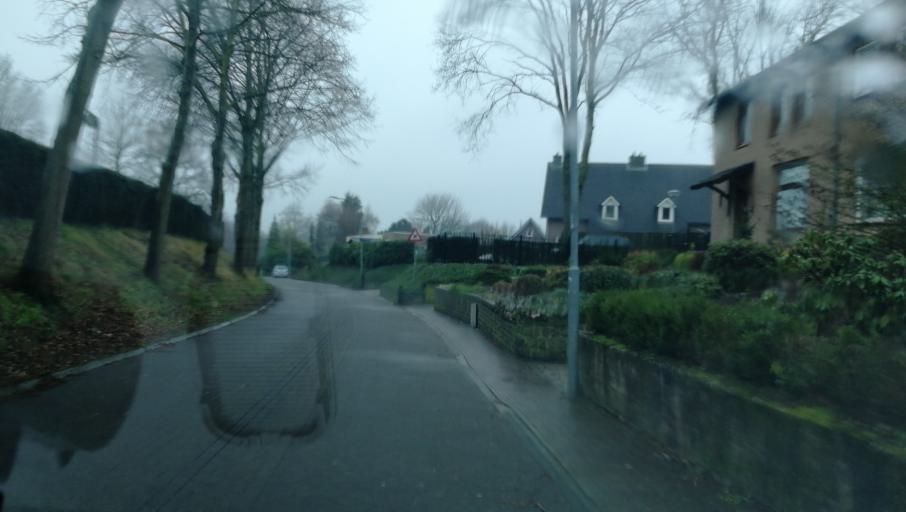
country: NL
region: Limburg
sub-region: Gemeente Venlo
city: Tegelen
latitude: 51.3576
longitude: 6.1281
